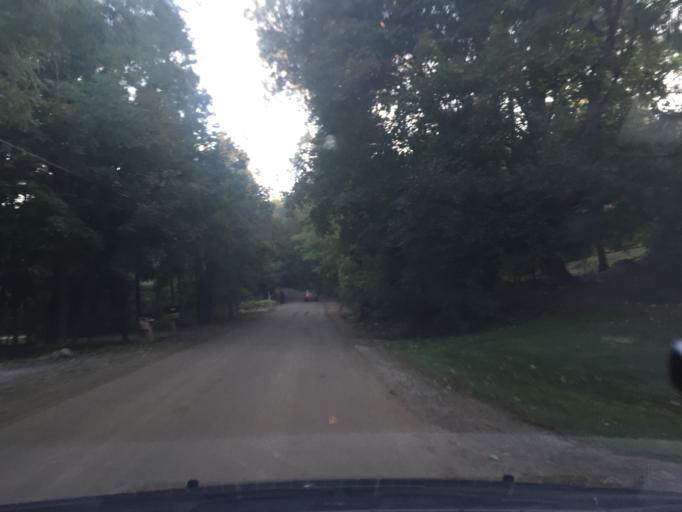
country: US
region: Michigan
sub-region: Oakland County
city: Bloomfield Hills
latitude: 42.5761
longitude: -83.2923
